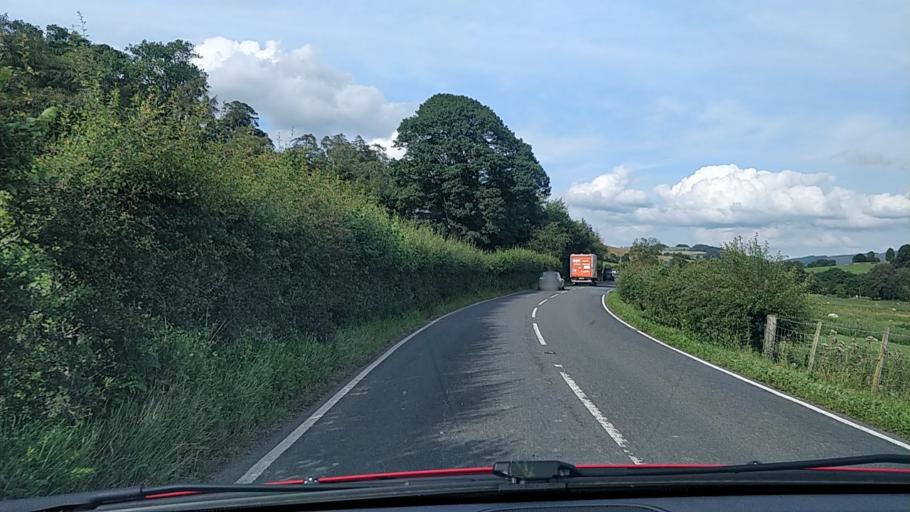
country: GB
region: Wales
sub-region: Denbighshire
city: Bryneglwys
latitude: 53.0151
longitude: -3.2850
